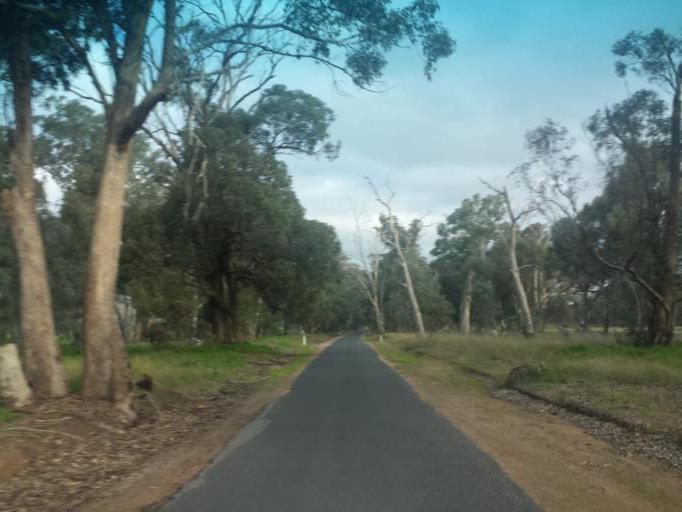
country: AU
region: Victoria
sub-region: Murrindindi
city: Kinglake West
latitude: -36.9202
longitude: 145.2254
